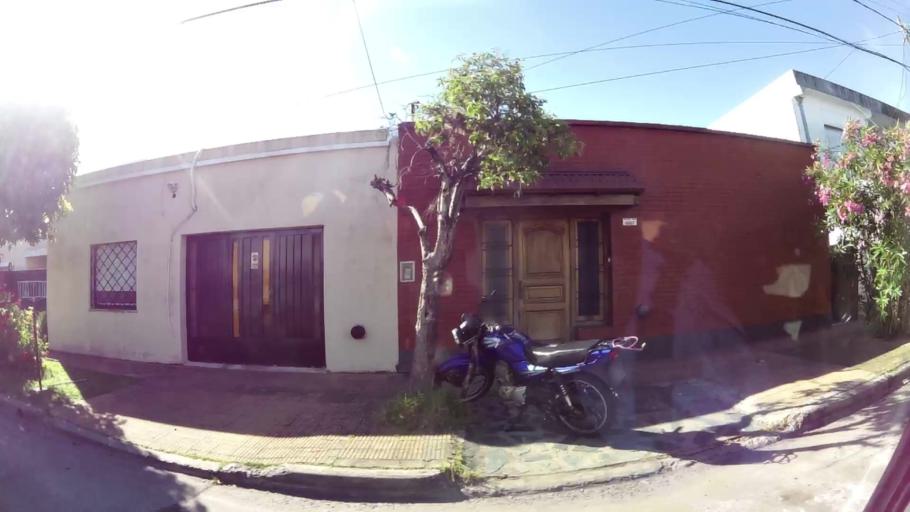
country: AR
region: Buenos Aires
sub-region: Partido de San Isidro
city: San Isidro
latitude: -34.4782
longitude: -58.5391
